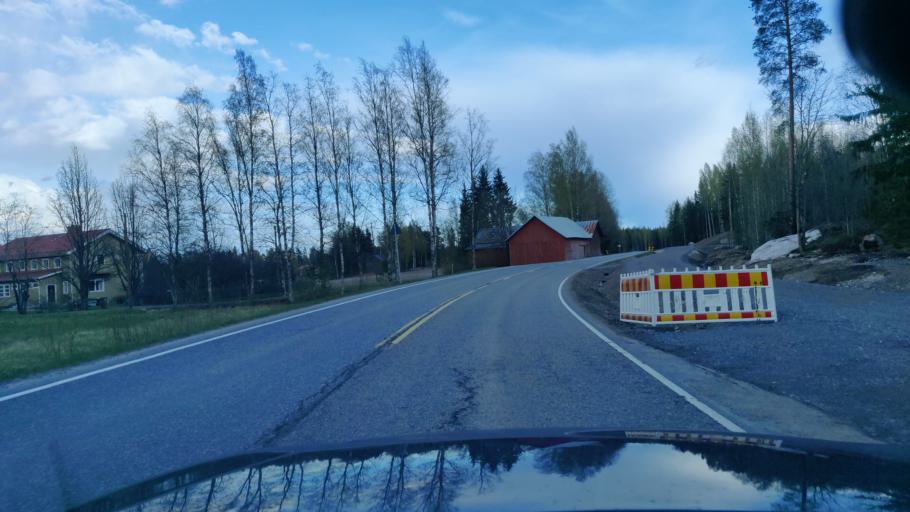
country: FI
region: Uusimaa
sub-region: Helsinki
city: Jaervenpaeae
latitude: 60.4825
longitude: 25.0565
